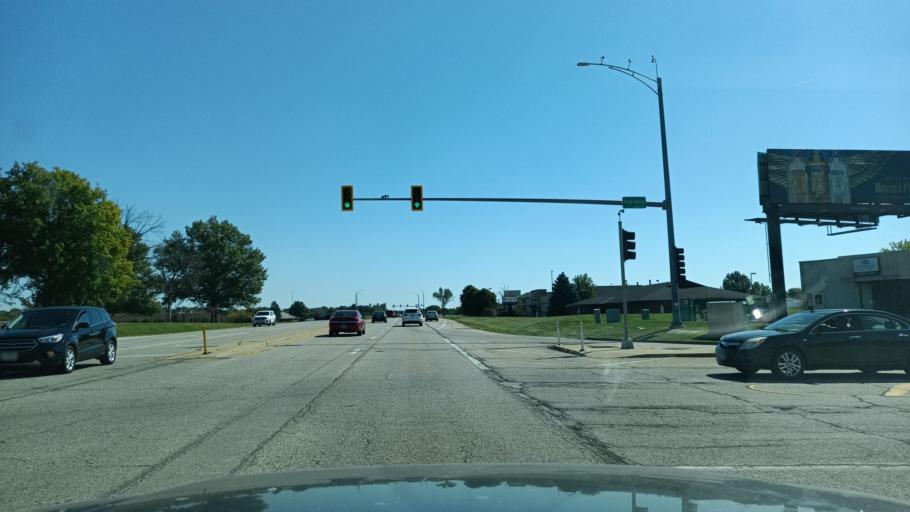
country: US
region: Illinois
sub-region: Peoria County
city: West Peoria
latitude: 40.7723
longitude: -89.6607
